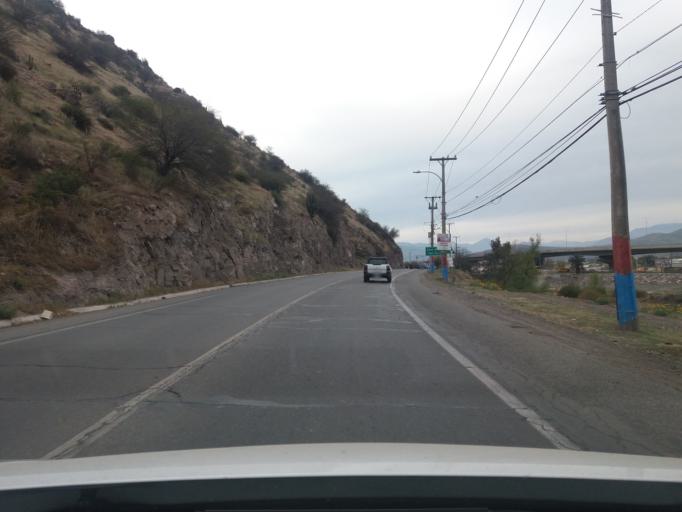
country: CL
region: Valparaiso
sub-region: Provincia de San Felipe
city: San Felipe
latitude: -32.7598
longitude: -70.7364
